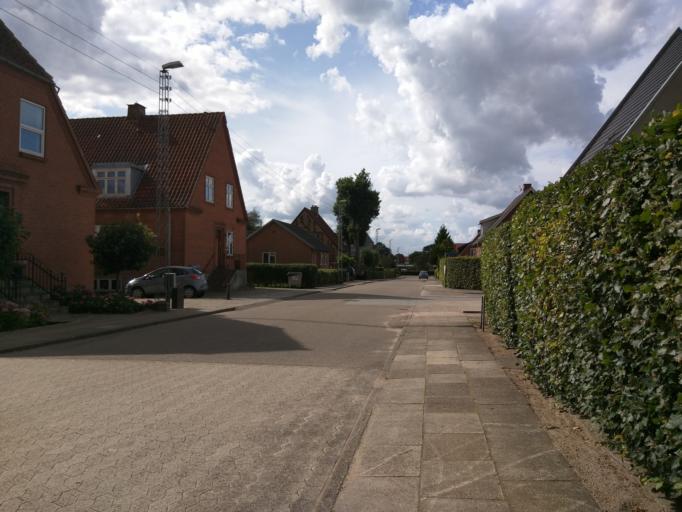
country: DK
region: Central Jutland
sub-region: Viborg Kommune
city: Viborg
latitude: 56.4561
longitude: 9.3985
